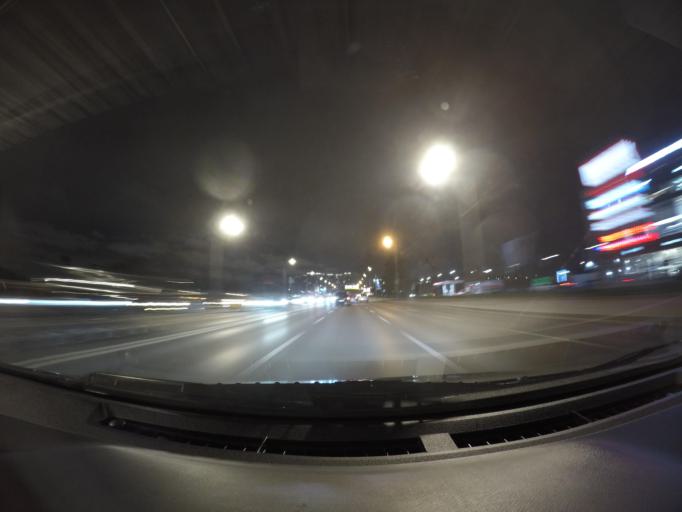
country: RU
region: Moscow
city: Tekstil'shchiki
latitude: 55.7148
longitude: 37.7139
